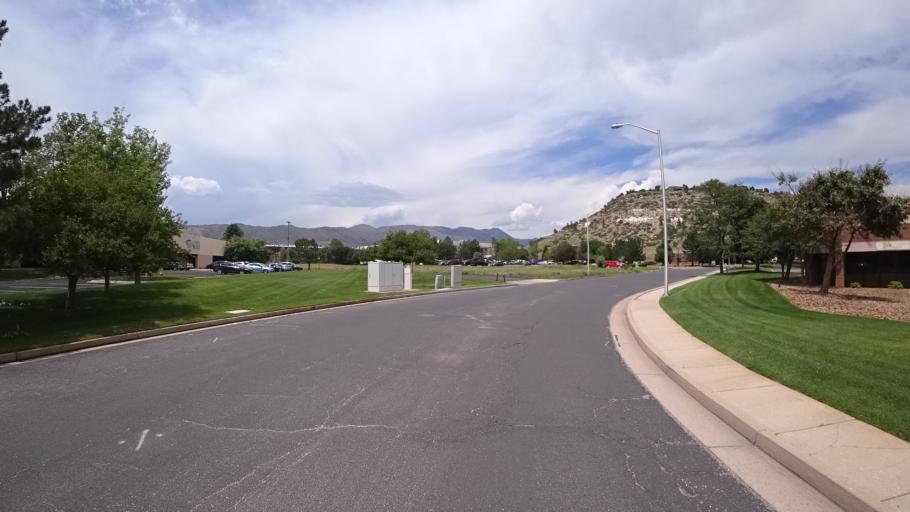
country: US
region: Colorado
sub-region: El Paso County
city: Colorado Springs
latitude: 38.8985
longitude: -104.8470
